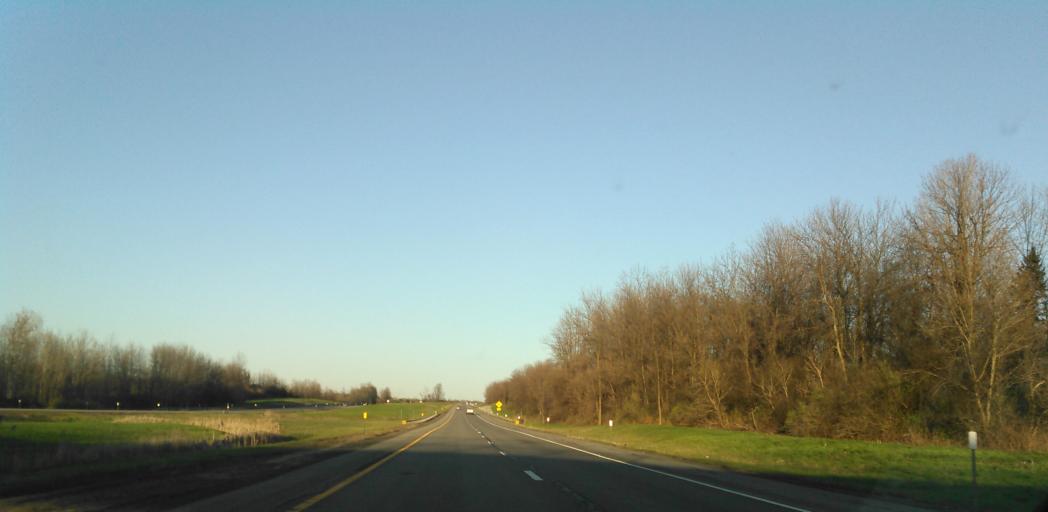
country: US
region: New York
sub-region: Monroe County
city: Pittsford
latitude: 43.0472
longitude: -77.5991
